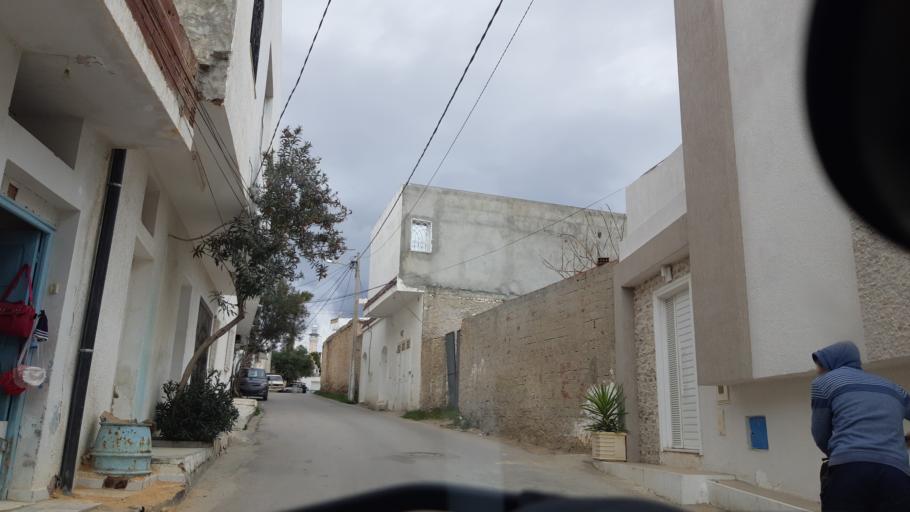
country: TN
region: Susah
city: Akouda
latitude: 35.8682
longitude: 10.5377
